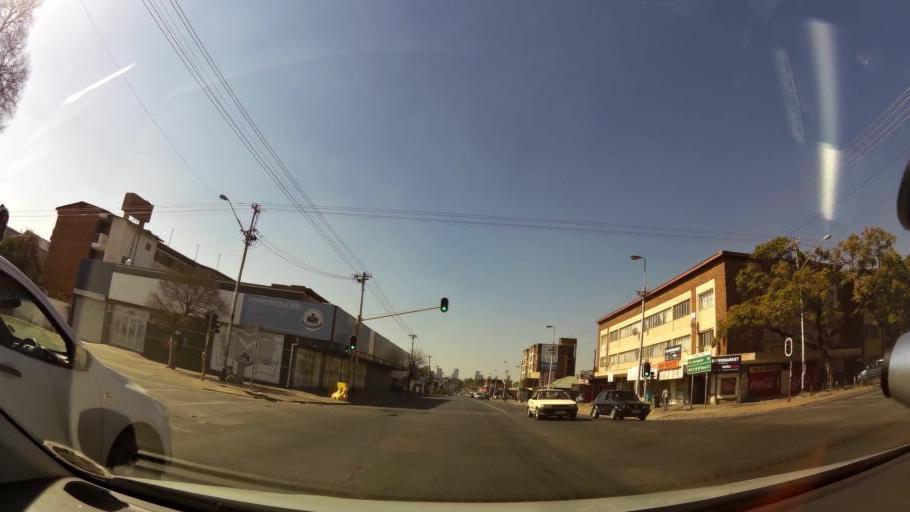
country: ZA
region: Gauteng
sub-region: City of Tshwane Metropolitan Municipality
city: Pretoria
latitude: -25.7489
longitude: 28.1523
